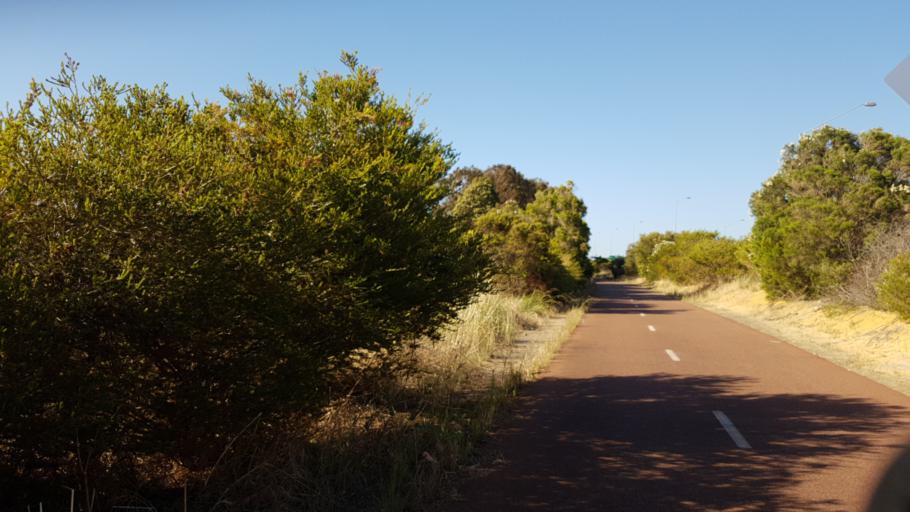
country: AU
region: Western Australia
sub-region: Kwinana
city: Wellard
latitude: -32.2973
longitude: 115.8342
